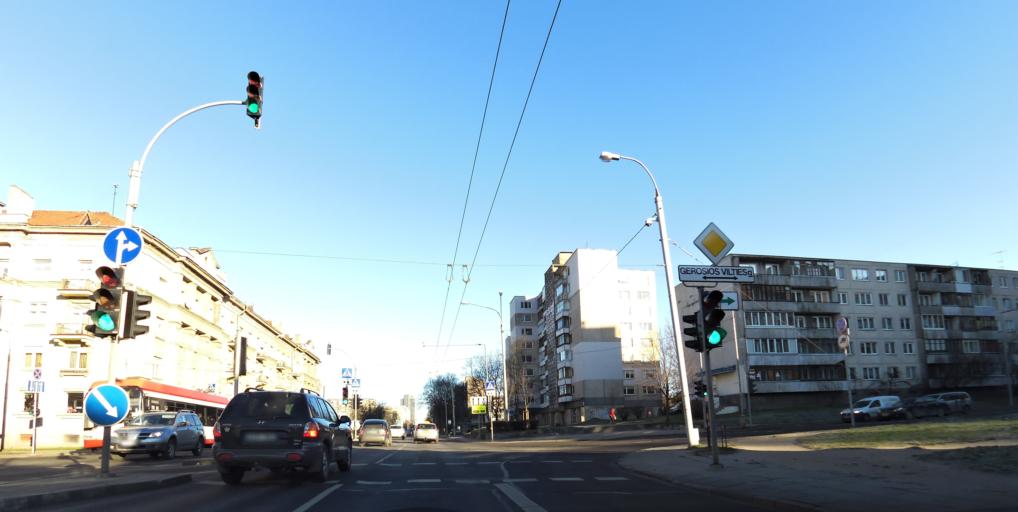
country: LT
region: Vilnius County
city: Vilkpede
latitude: 54.6712
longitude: 25.2429
